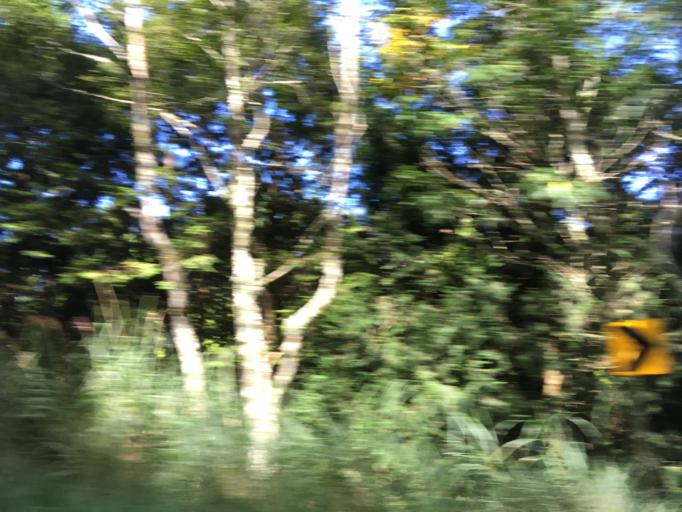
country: TW
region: Taiwan
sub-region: Yilan
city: Yilan
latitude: 24.5129
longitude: 121.5897
